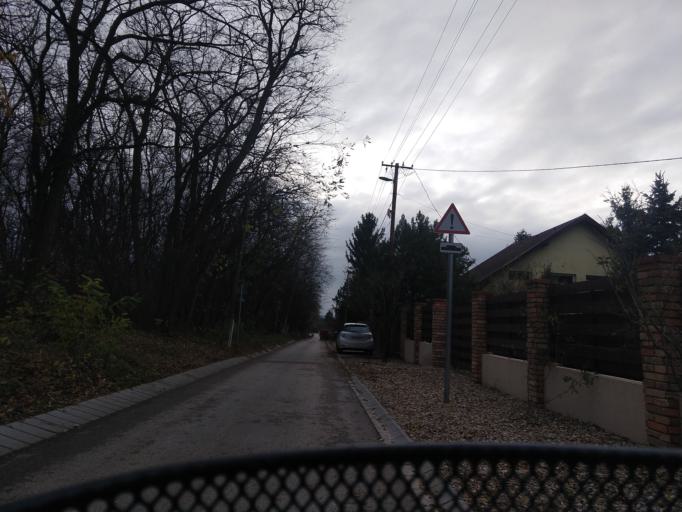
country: HU
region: Pest
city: Veresegyhaz
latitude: 47.6495
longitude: 19.2694
